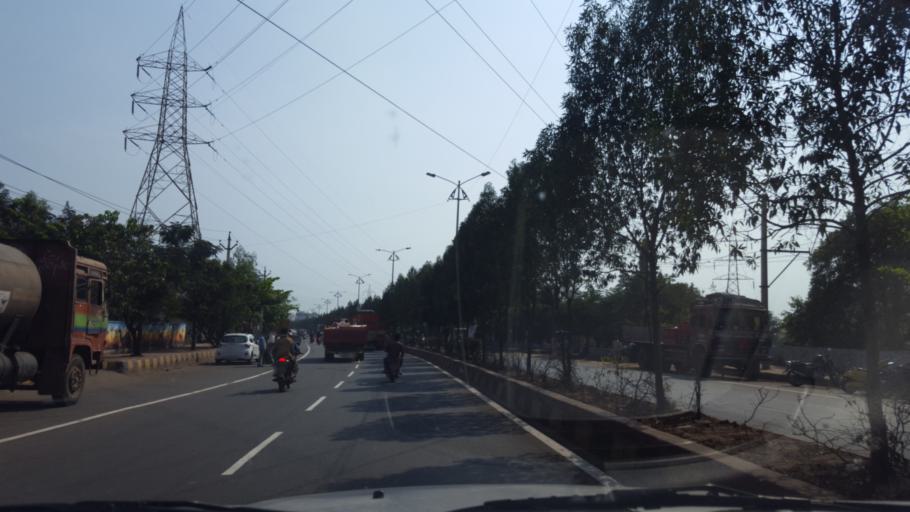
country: IN
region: Andhra Pradesh
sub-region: Vishakhapatnam
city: Visakhapatnam
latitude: 17.6829
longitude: 83.1938
